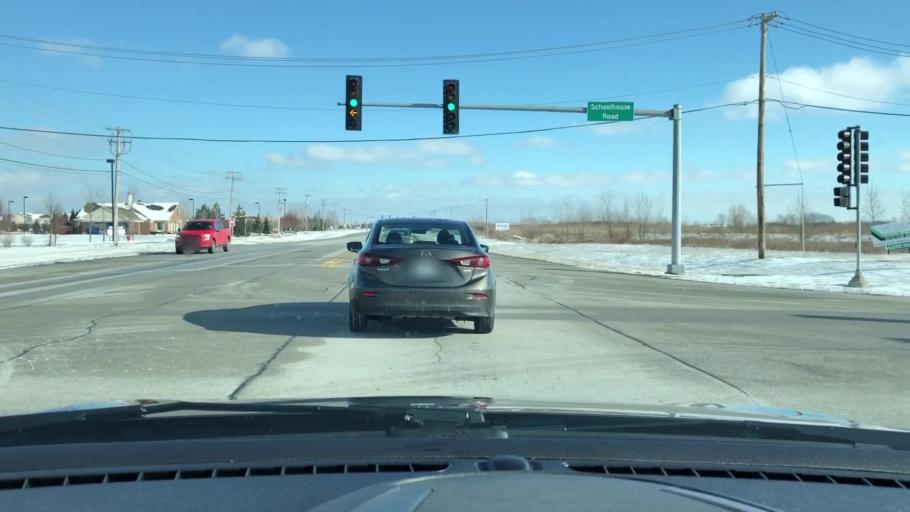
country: US
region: Illinois
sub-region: Will County
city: New Lenox
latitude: 41.4837
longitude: -87.9263
